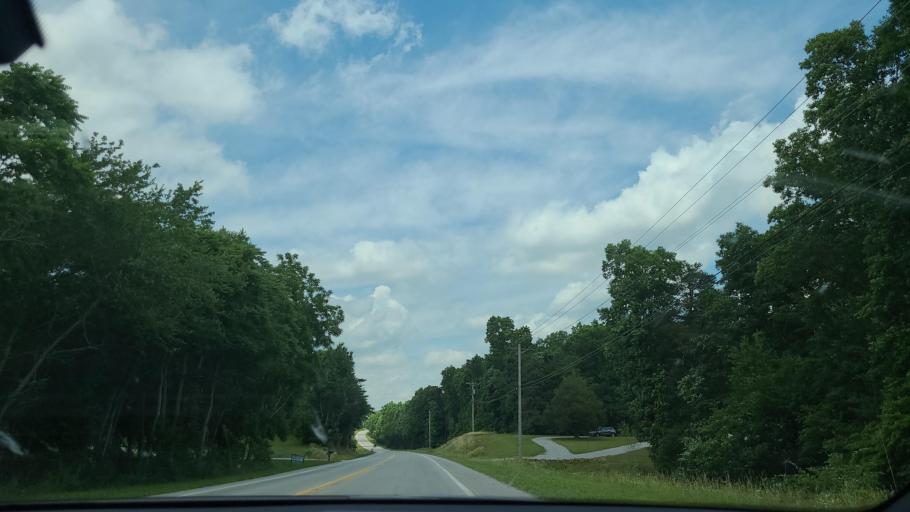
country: US
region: Tennessee
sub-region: Cumberland County
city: Lake Tansi
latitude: 35.8200
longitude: -85.0192
